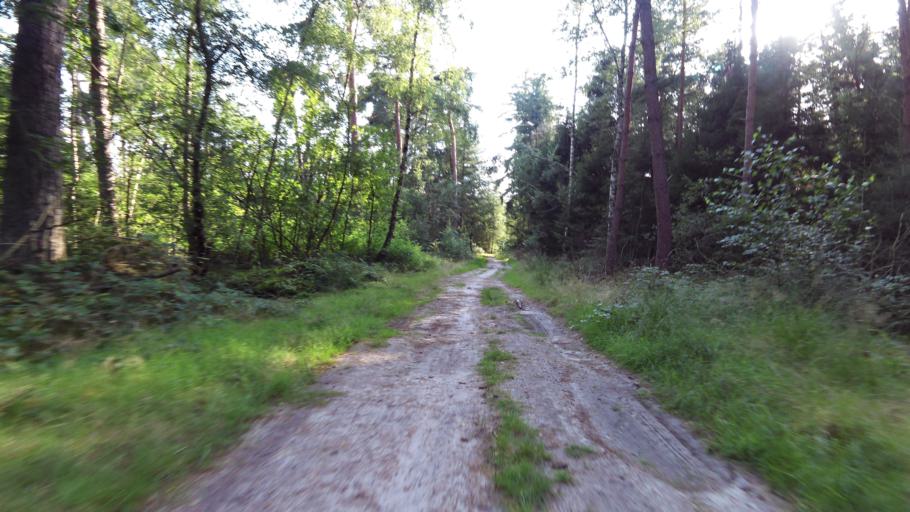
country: NL
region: Utrecht
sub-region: Gemeente Soest
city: Soest
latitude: 52.1561
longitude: 5.2719
